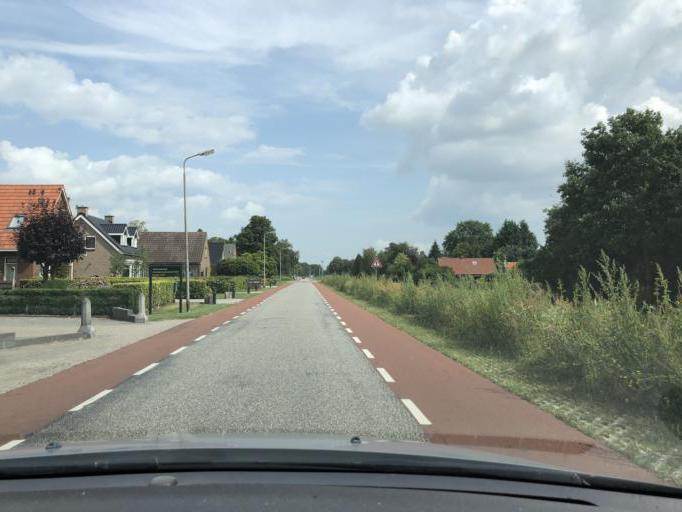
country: NL
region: Drenthe
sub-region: Gemeente Hoogeveen
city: Hoogeveen
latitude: 52.7621
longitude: 6.6045
